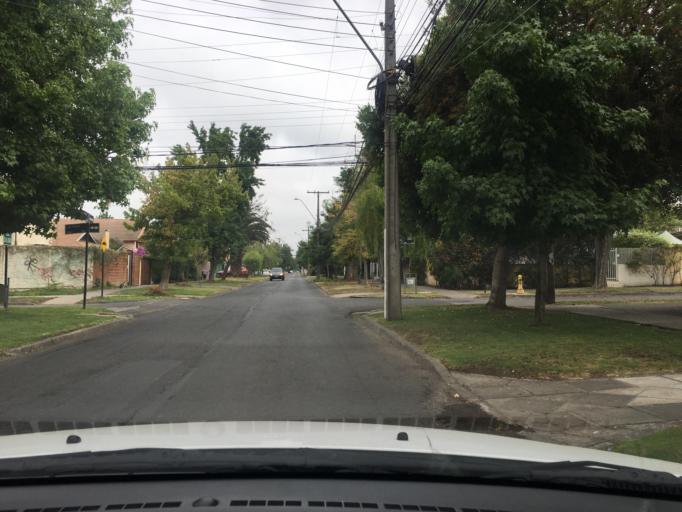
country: CL
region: Santiago Metropolitan
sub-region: Provincia de Santiago
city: Villa Presidente Frei, Nunoa, Santiago, Chile
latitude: -33.4551
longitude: -70.5549
